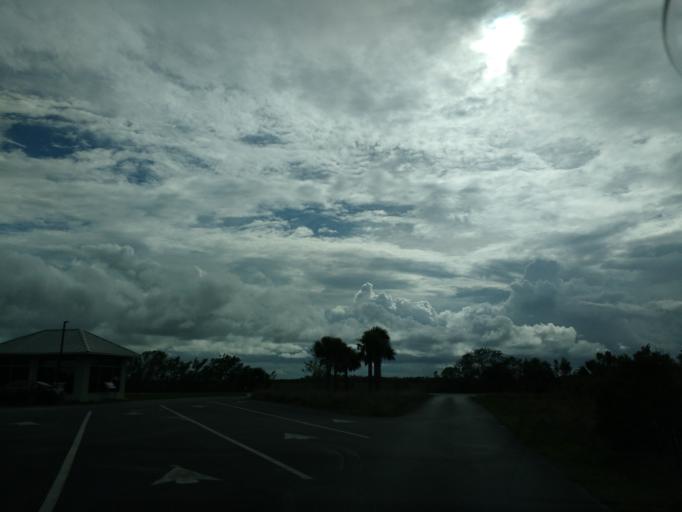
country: US
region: Florida
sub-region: Collier County
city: Marco
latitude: 25.9009
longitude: -81.3259
